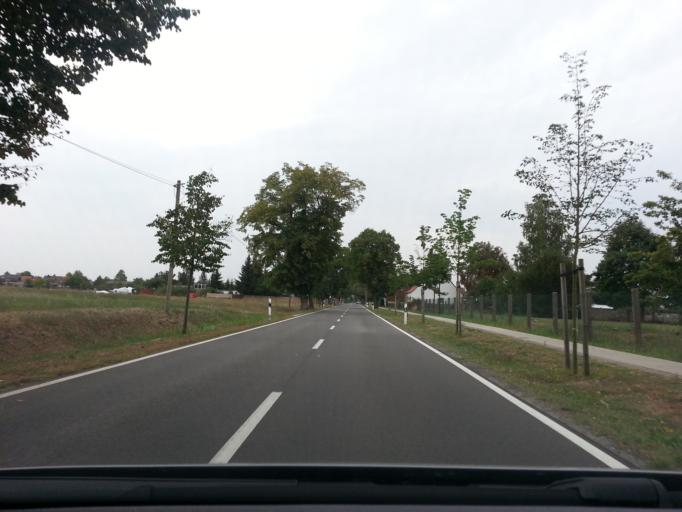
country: DE
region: Mecklenburg-Vorpommern
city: Ferdinandshof
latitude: 53.7066
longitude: 13.9432
